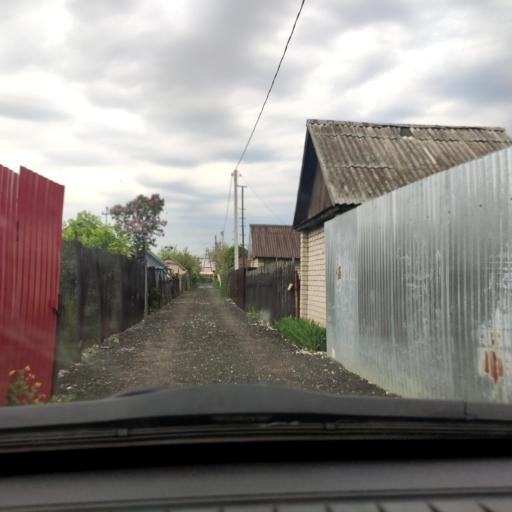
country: RU
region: Samara
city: Tol'yatti
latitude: 53.5441
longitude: 49.4390
